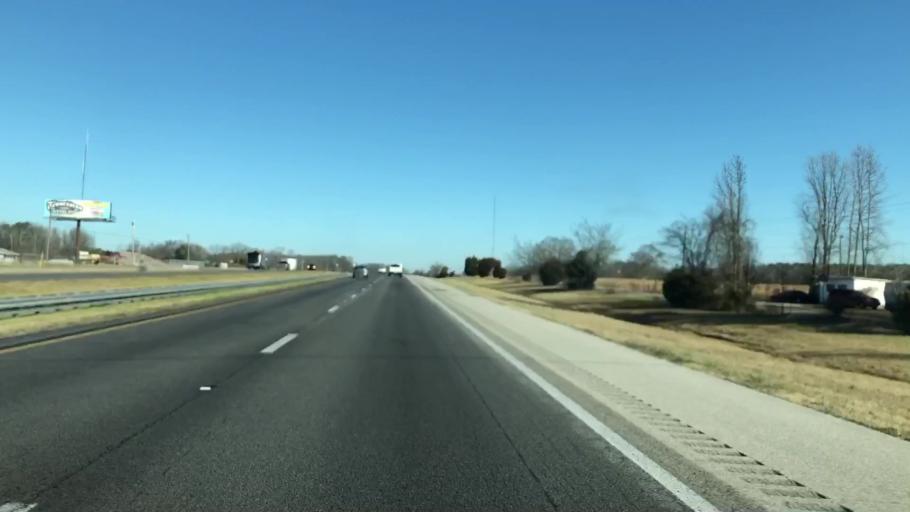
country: US
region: Alabama
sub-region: Limestone County
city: Athens
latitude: 34.8765
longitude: -86.9208
